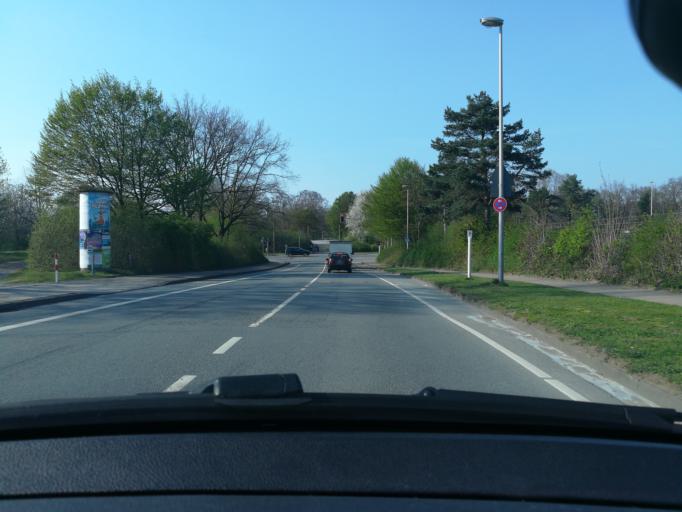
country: DE
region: North Rhine-Westphalia
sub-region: Regierungsbezirk Detmold
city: Bielefeld
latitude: 51.9808
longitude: 8.4981
